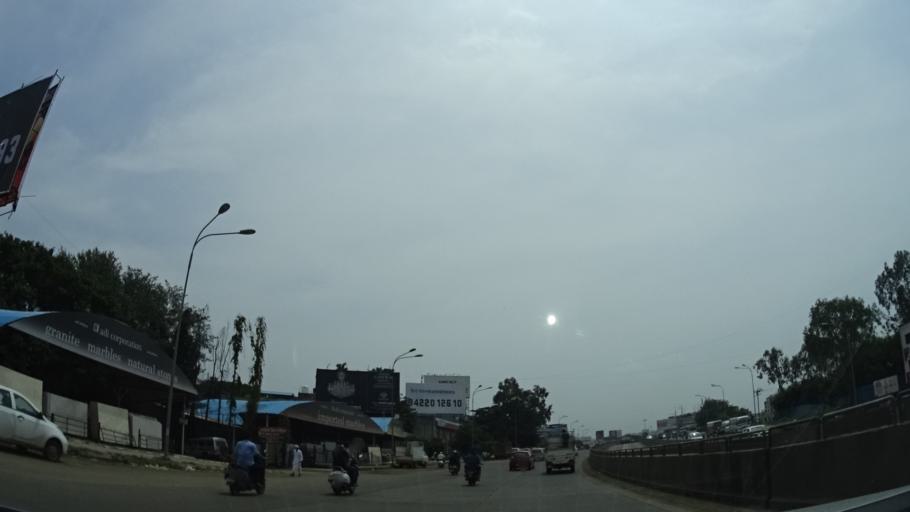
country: IN
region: Maharashtra
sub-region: Pune Division
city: Lohogaon
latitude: 18.5634
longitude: 73.9352
